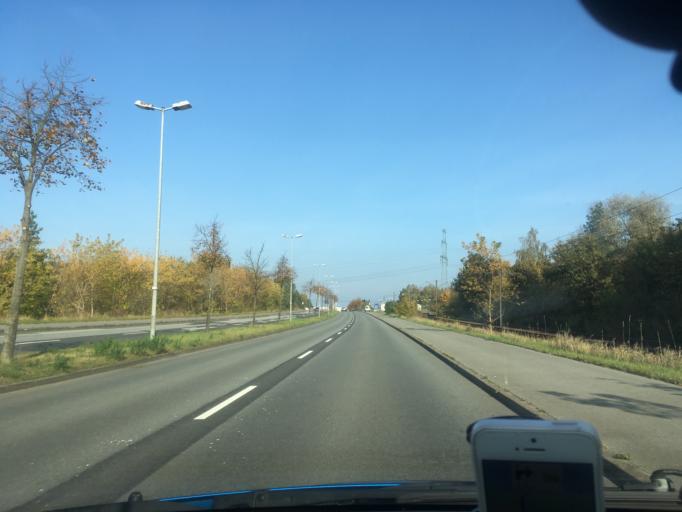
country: DE
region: Mecklenburg-Vorpommern
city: Feldstadt
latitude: 53.5813
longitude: 11.3994
